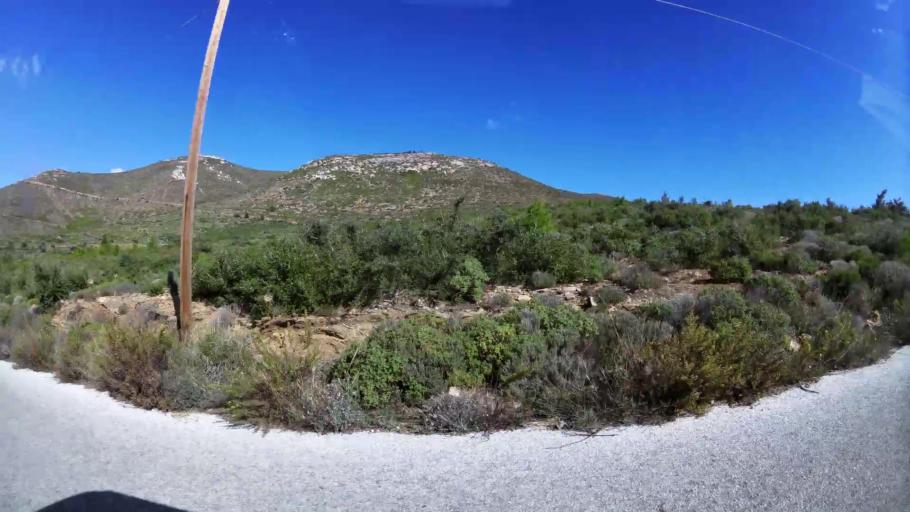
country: GR
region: Attica
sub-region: Nomarchia Anatolikis Attikis
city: Dioni
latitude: 38.0378
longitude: 23.9272
